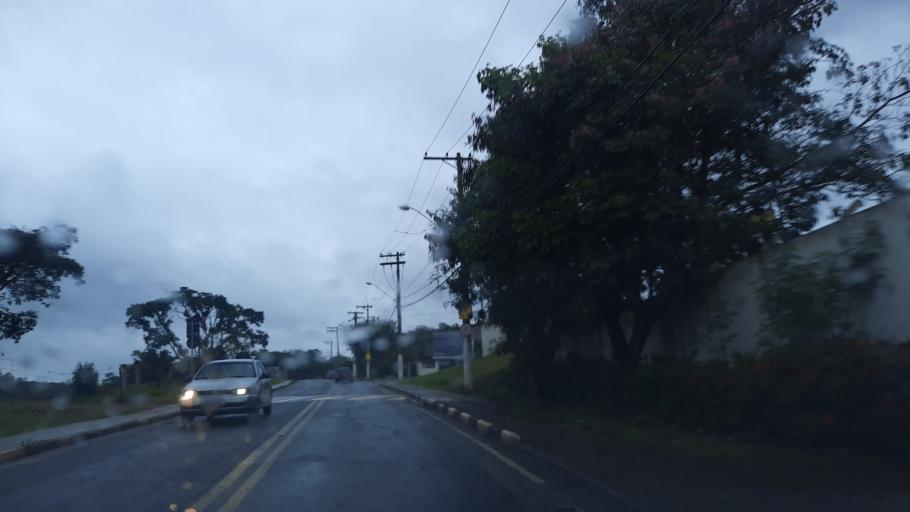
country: BR
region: Sao Paulo
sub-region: Atibaia
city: Atibaia
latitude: -23.0966
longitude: -46.5486
